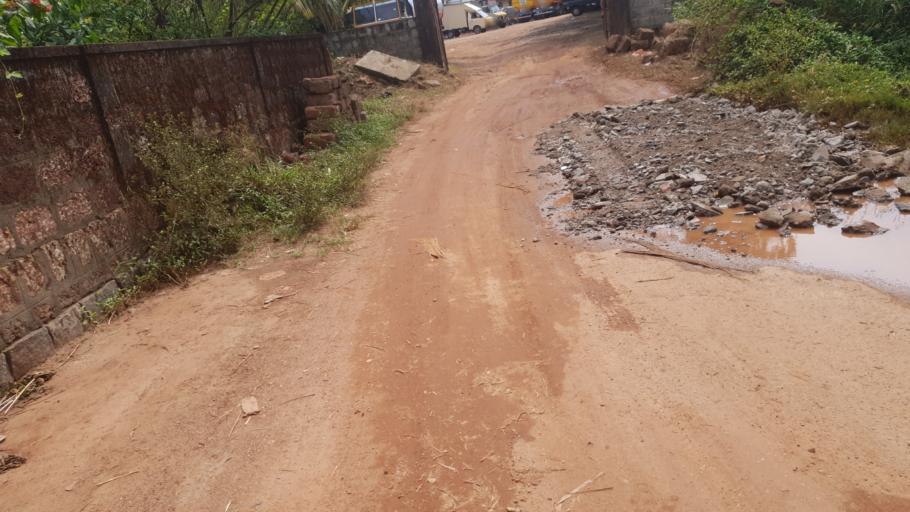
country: IN
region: Karnataka
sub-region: Dakshina Kannada
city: Ullal
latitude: 12.8426
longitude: 74.8474
